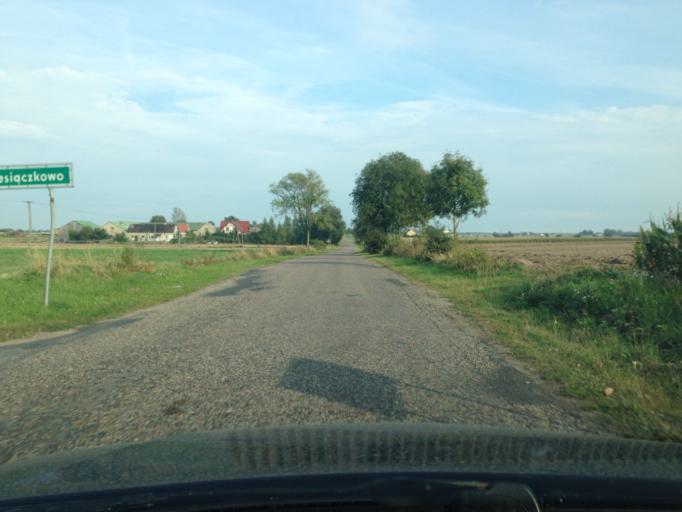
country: PL
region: Kujawsko-Pomorskie
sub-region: Powiat brodnicki
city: Bartniczka
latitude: 53.2086
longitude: 19.5806
